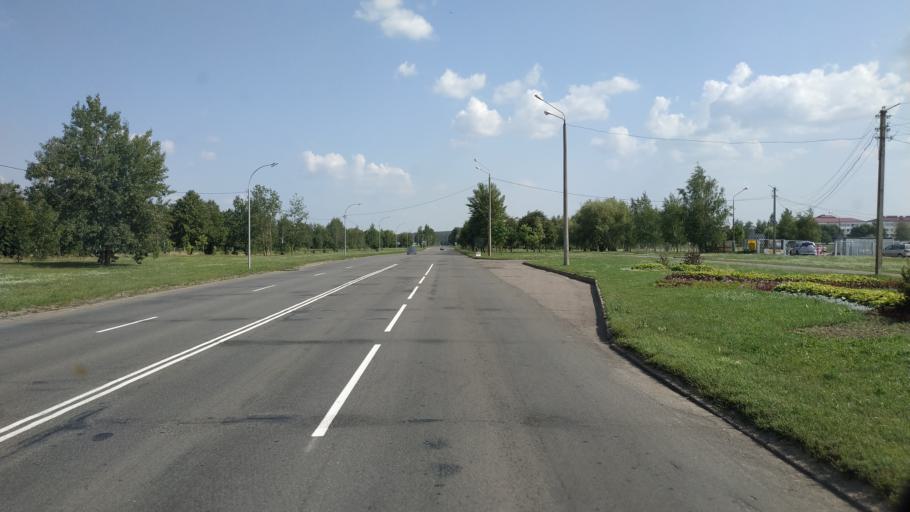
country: BY
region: Mogilev
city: Buynichy
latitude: 53.8604
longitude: 30.3244
